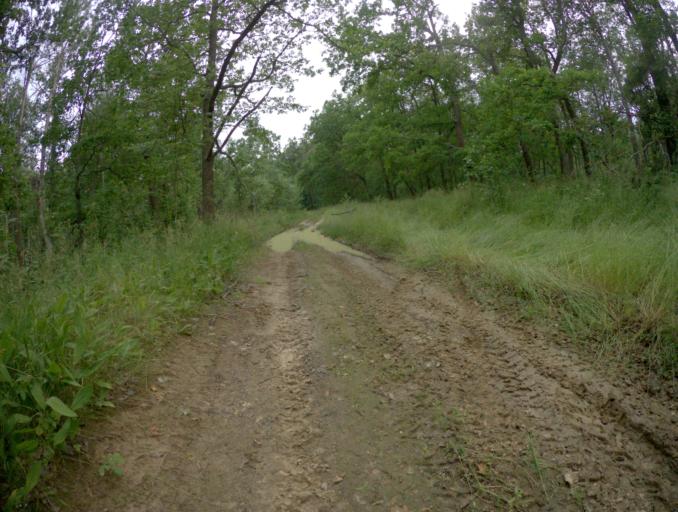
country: RU
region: Vladimir
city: Gorokhovets
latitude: 56.2256
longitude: 42.6728
